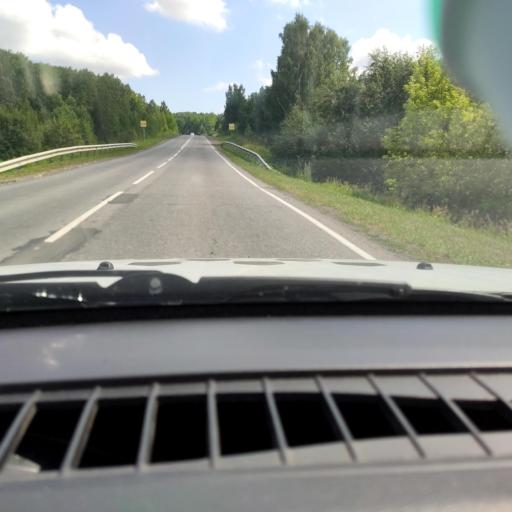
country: RU
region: Bashkortostan
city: Verkhniye Kigi
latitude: 55.3881
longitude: 58.6627
